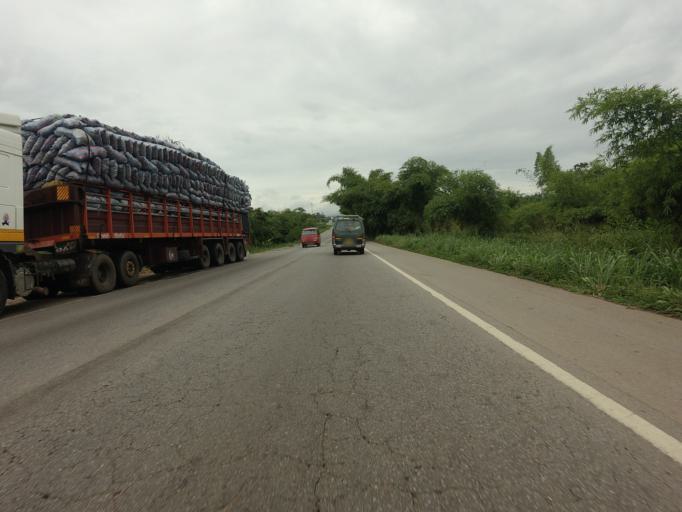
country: GH
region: Eastern
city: Begoro
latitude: 6.3971
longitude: -0.5602
